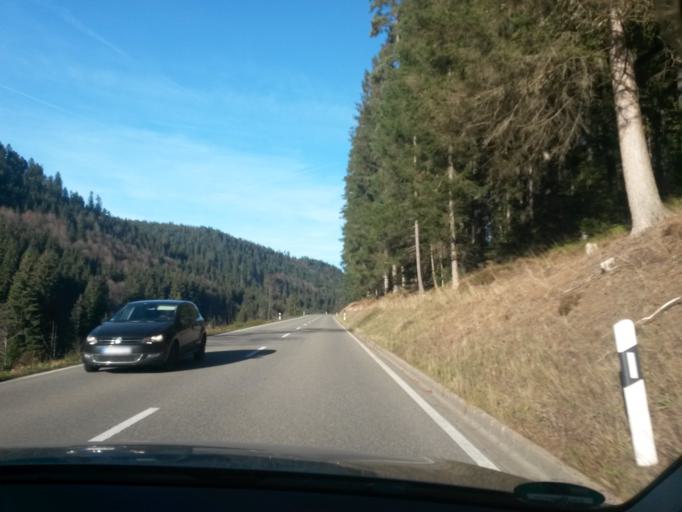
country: DE
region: Baden-Wuerttemberg
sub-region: Karlsruhe Region
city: Neuweiler
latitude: 48.6759
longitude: 8.5626
